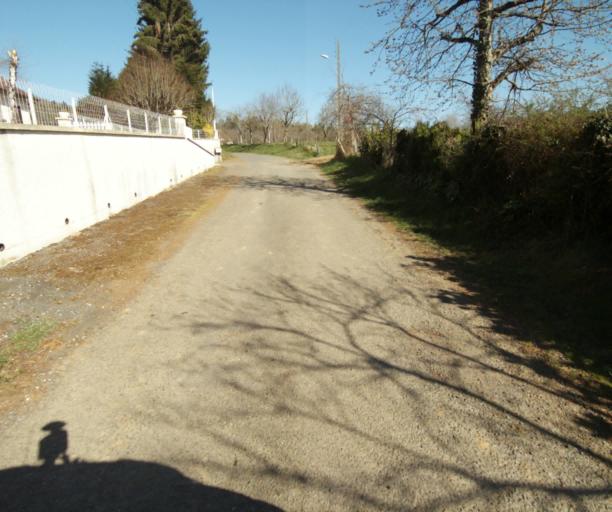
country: FR
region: Limousin
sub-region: Departement de la Correze
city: Tulle
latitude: 45.2890
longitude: 1.7290
